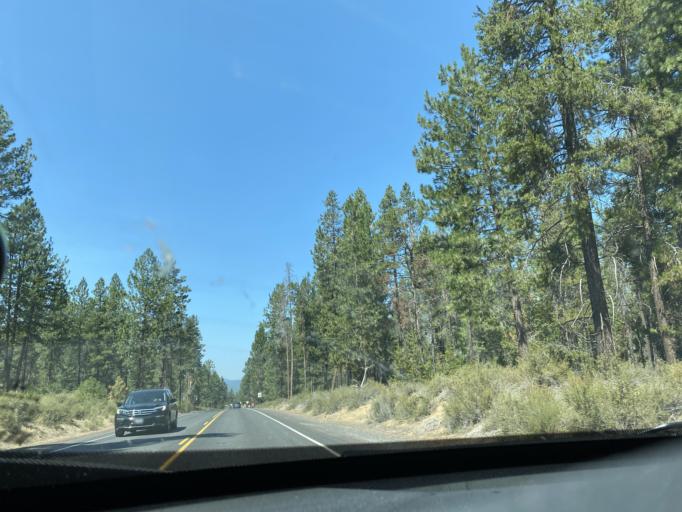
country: US
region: Oregon
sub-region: Deschutes County
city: Sunriver
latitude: 43.8921
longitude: -121.4086
